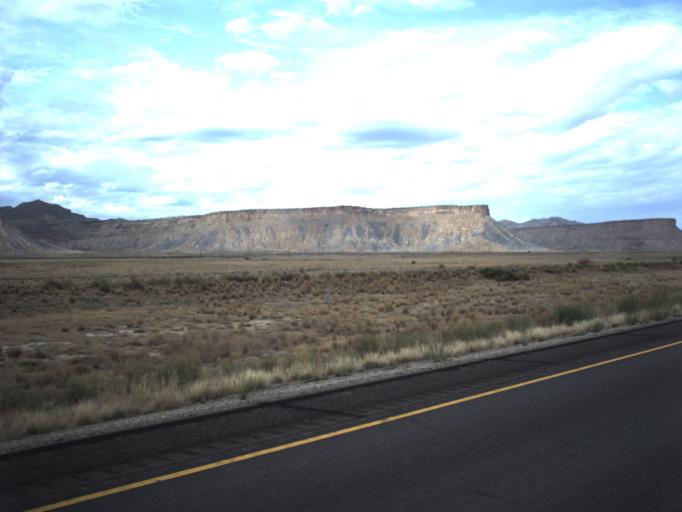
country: US
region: Utah
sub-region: Grand County
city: Moab
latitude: 38.9528
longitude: -109.7625
